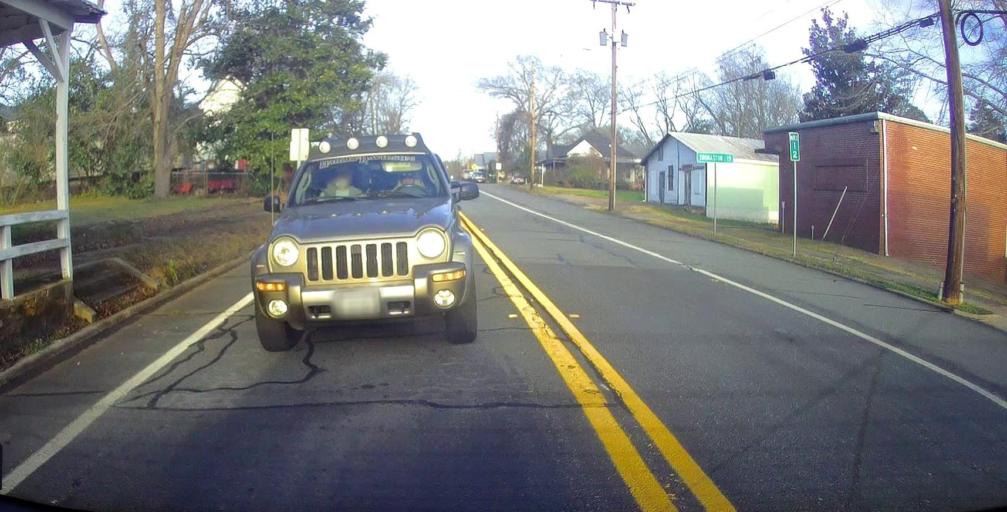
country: US
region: Georgia
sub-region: Talbot County
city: Sardis
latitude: 32.7878
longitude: -84.5604
